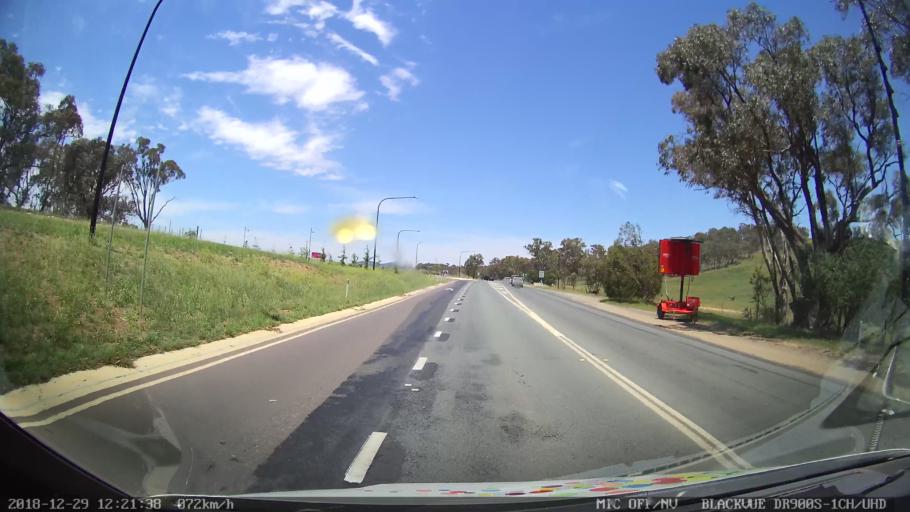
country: AU
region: New South Wales
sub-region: Queanbeyan
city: Queanbeyan
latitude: -35.4157
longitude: 149.2227
